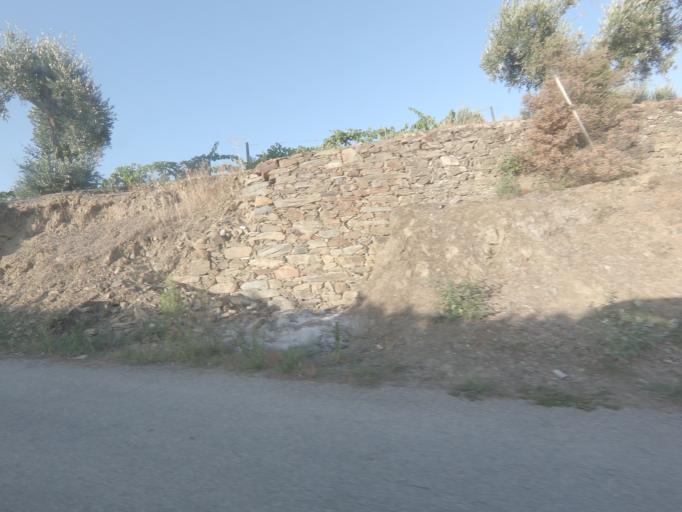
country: PT
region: Viseu
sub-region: Armamar
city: Armamar
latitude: 41.1437
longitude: -7.6783
